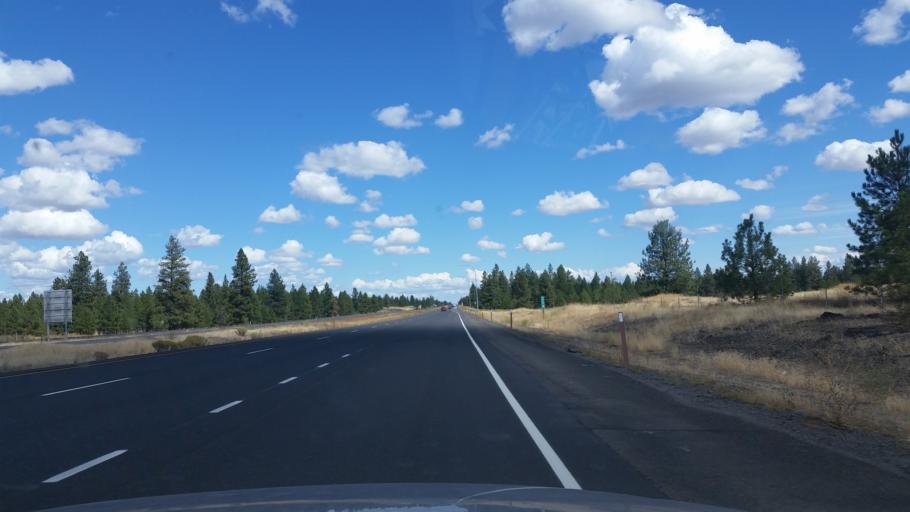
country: US
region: Washington
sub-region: Spokane County
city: Medical Lake
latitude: 47.4388
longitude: -117.7865
